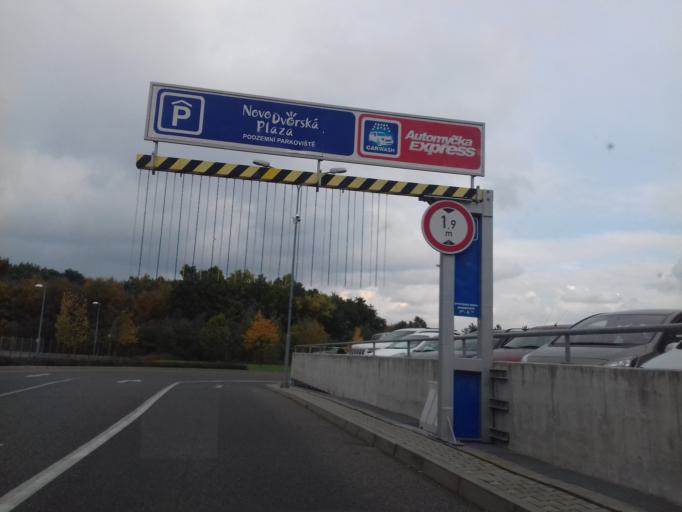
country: CZ
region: Praha
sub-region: Praha 4
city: Hodkovicky
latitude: 50.0275
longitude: 14.4322
